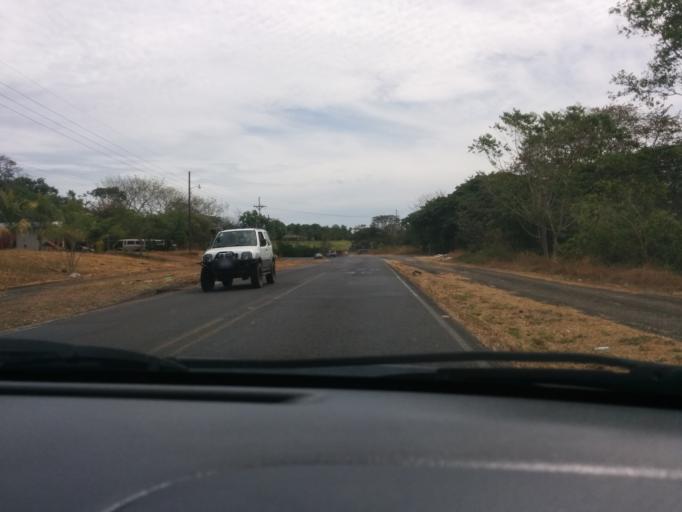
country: CR
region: Puntarenas
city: Esparza
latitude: 10.0027
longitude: -84.6224
